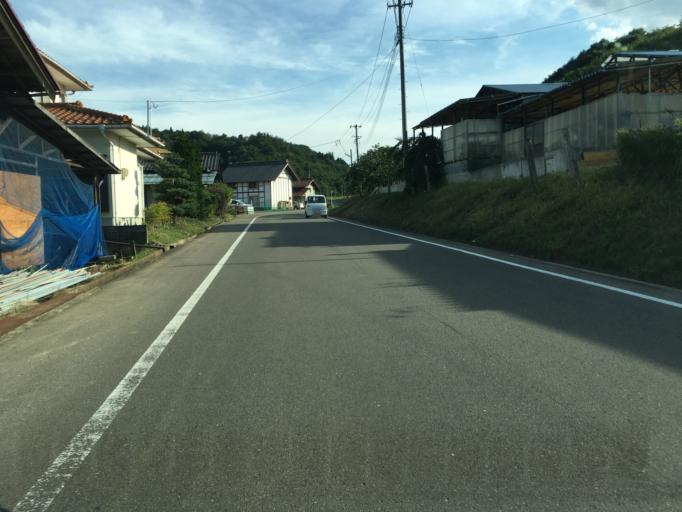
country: JP
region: Fukushima
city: Yanagawamachi-saiwaicho
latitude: 37.8157
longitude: 140.5891
